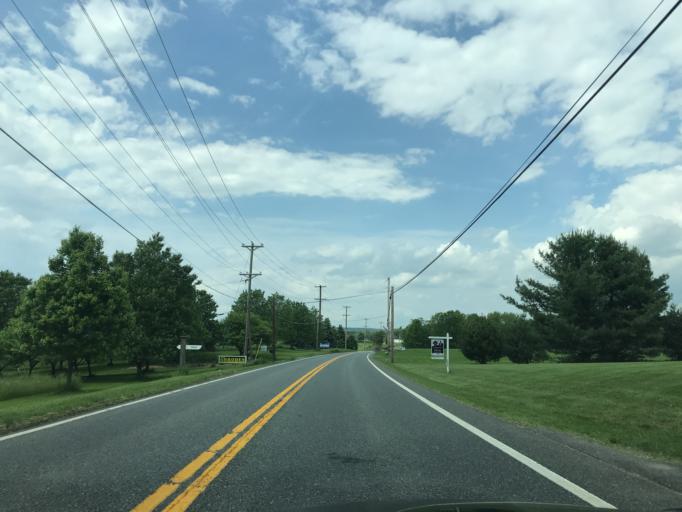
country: US
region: Maryland
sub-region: Harford County
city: Bel Air North
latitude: 39.6442
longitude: -76.3345
